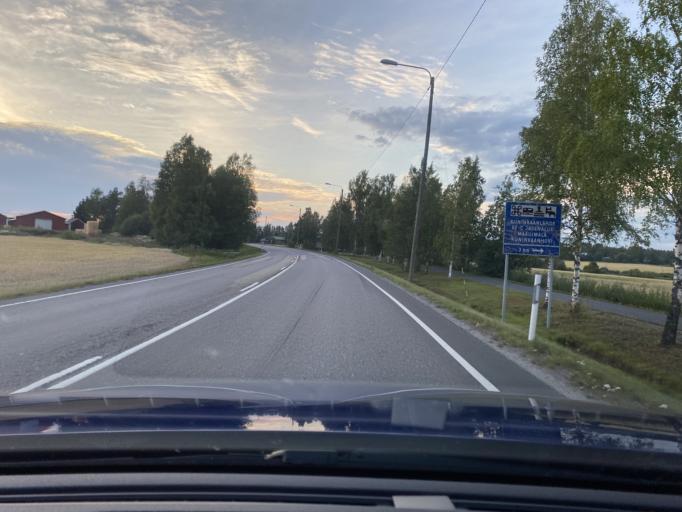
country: FI
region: Satakunta
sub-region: Pohjois-Satakunta
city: Kankaanpaeae
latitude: 61.7599
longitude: 22.5029
